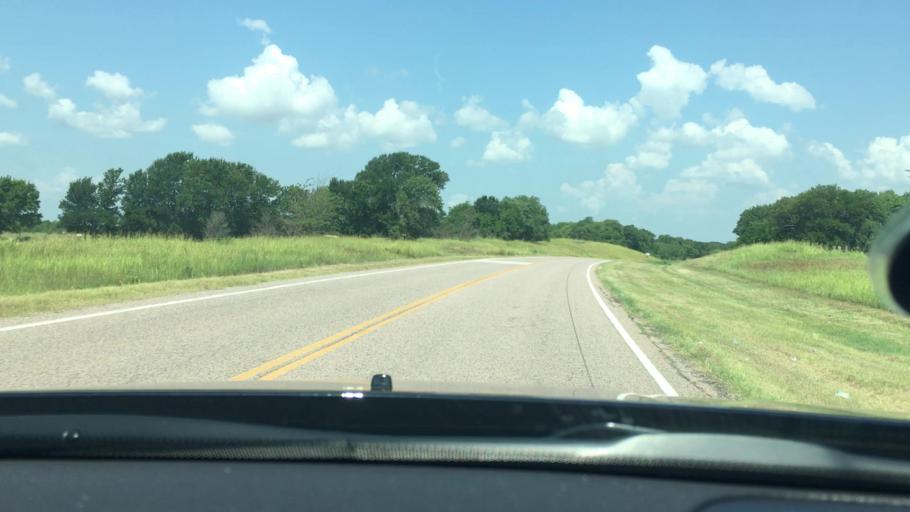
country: US
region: Oklahoma
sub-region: Bryan County
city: Durant
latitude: 34.0812
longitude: -96.3757
